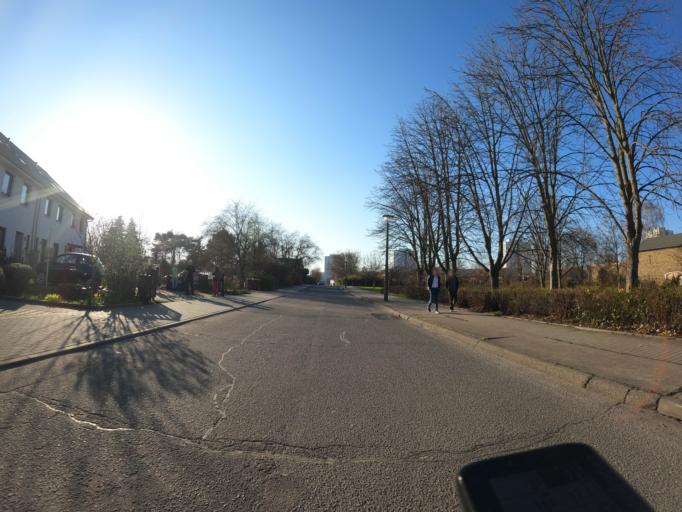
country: DE
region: Berlin
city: Marzahn
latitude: 52.5426
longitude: 13.5589
